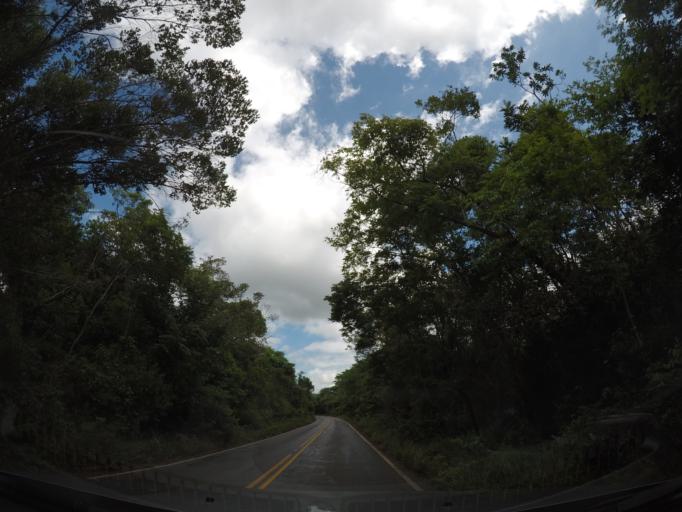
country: BR
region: Bahia
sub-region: Andarai
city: Vera Cruz
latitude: -12.5097
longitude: -41.3615
